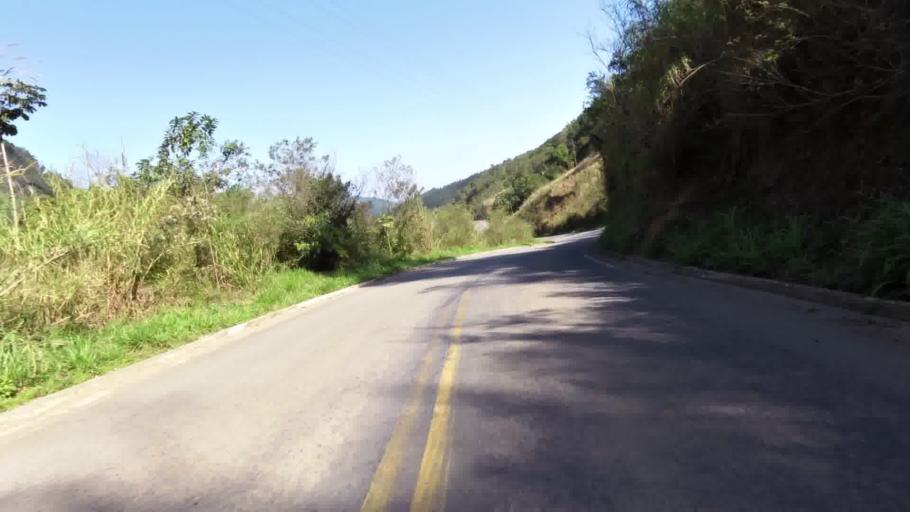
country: BR
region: Espirito Santo
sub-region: Marechal Floriano
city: Marechal Floriano
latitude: -20.5005
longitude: -40.7746
